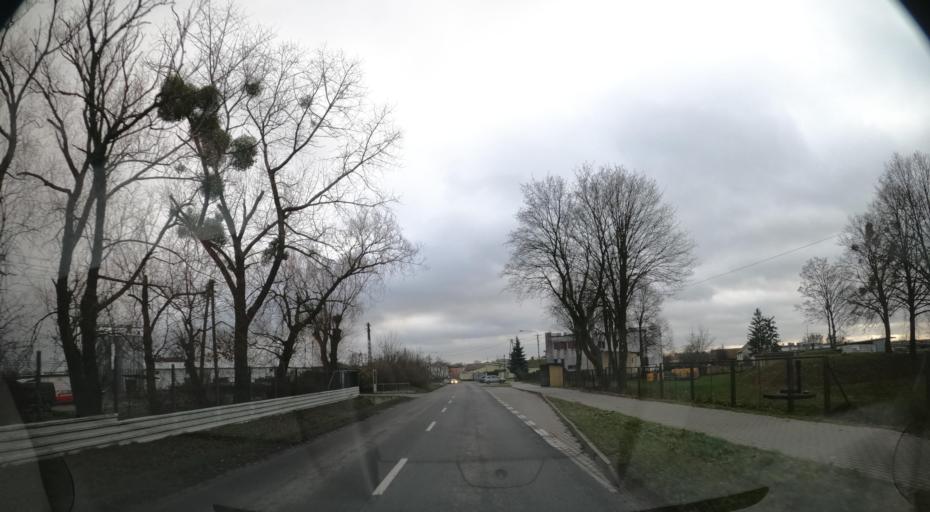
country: PL
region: Kujawsko-Pomorskie
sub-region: Powiat nakielski
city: Sadki
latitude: 53.1622
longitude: 17.4462
